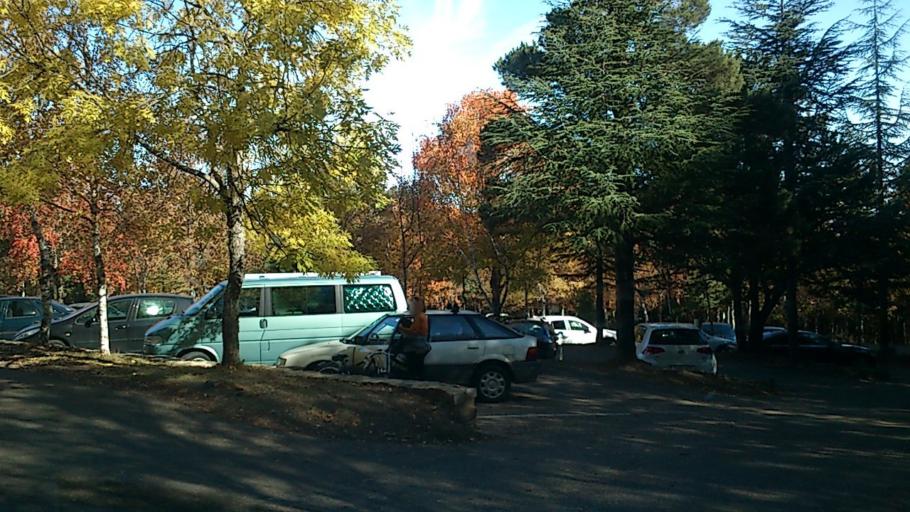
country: ES
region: Castille and Leon
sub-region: Provincia de Soria
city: Vozmediano
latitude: 41.8166
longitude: -1.8222
